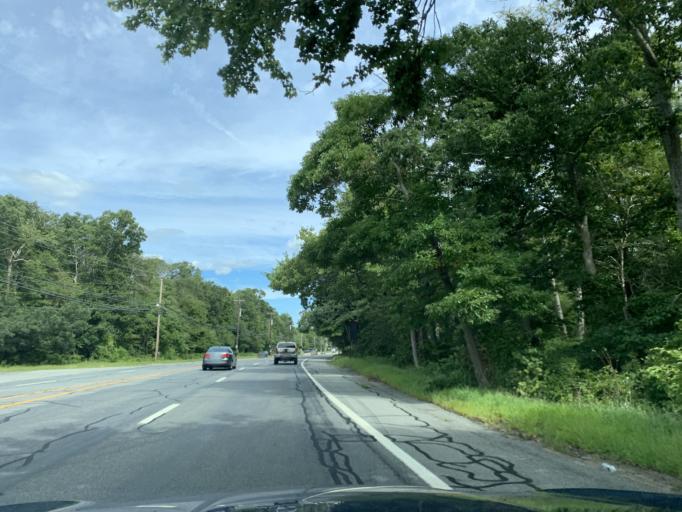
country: US
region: Rhode Island
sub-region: Kent County
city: West Greenwich
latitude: 41.5900
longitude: -71.6504
